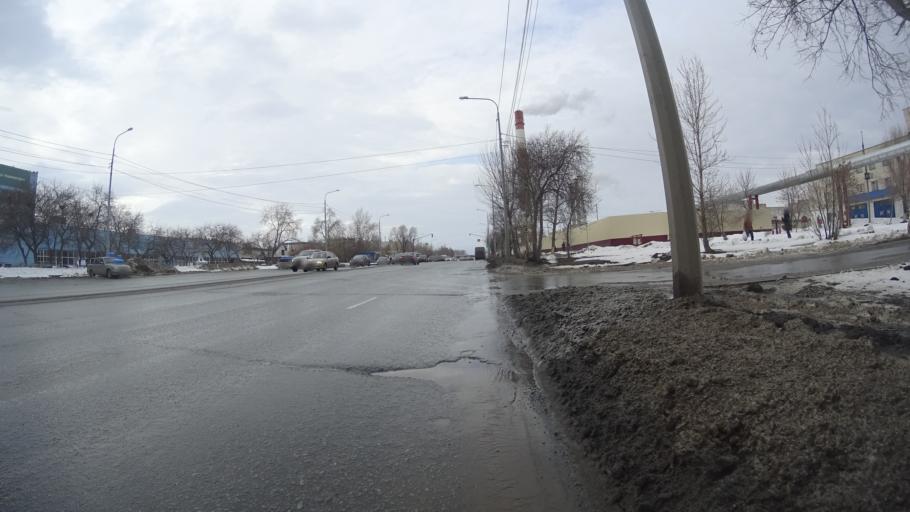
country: RU
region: Chelyabinsk
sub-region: Gorod Chelyabinsk
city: Chelyabinsk
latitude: 55.2045
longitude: 61.3233
